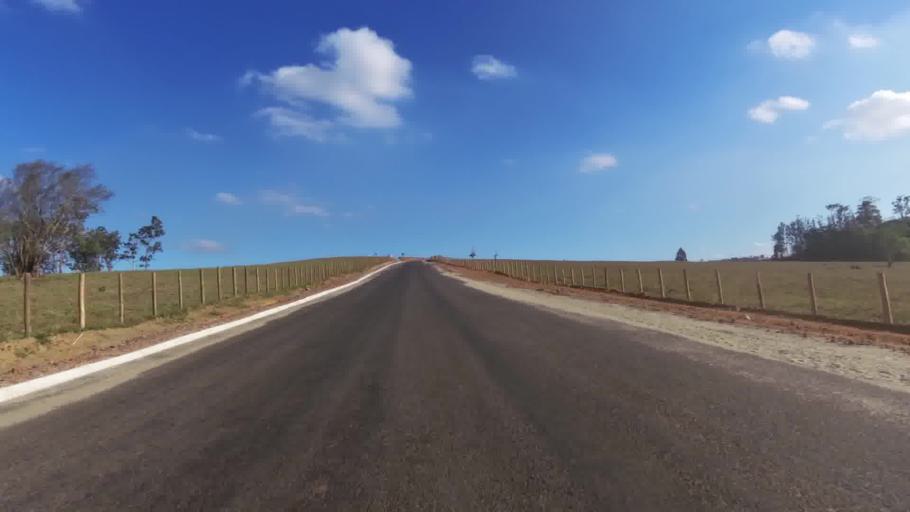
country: BR
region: Espirito Santo
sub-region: Marataizes
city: Marataizes
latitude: -21.1382
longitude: -41.0585
